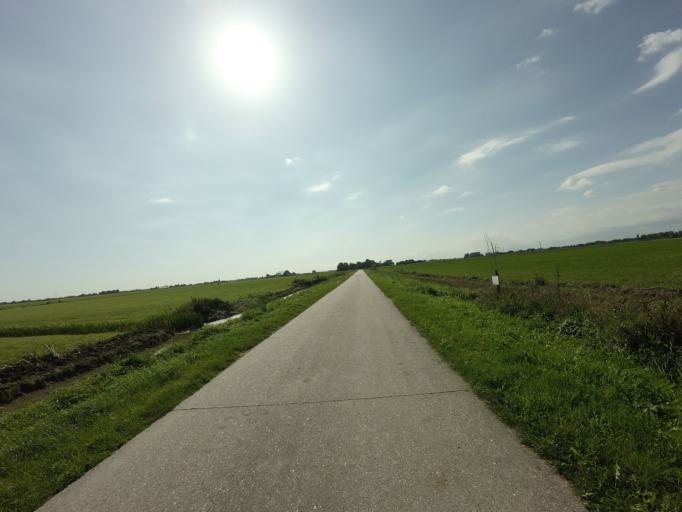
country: NL
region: Friesland
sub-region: Gemeente Littenseradiel
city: Makkum
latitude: 53.0975
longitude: 5.6483
